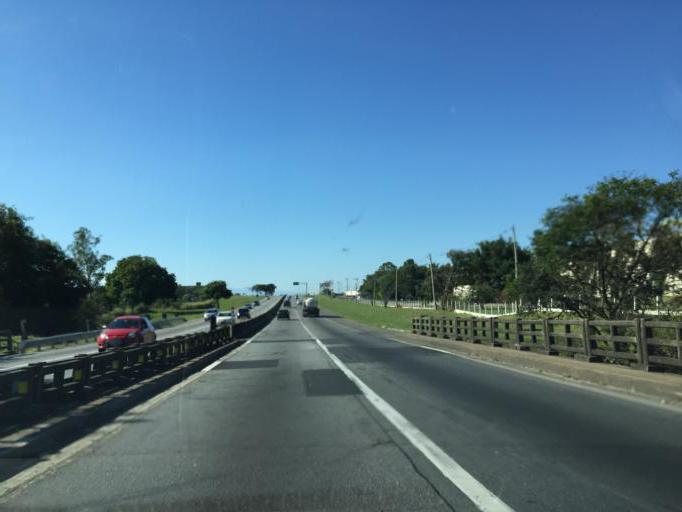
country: BR
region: Sao Paulo
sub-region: Lorena
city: Lorena
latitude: -22.7556
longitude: -45.1117
